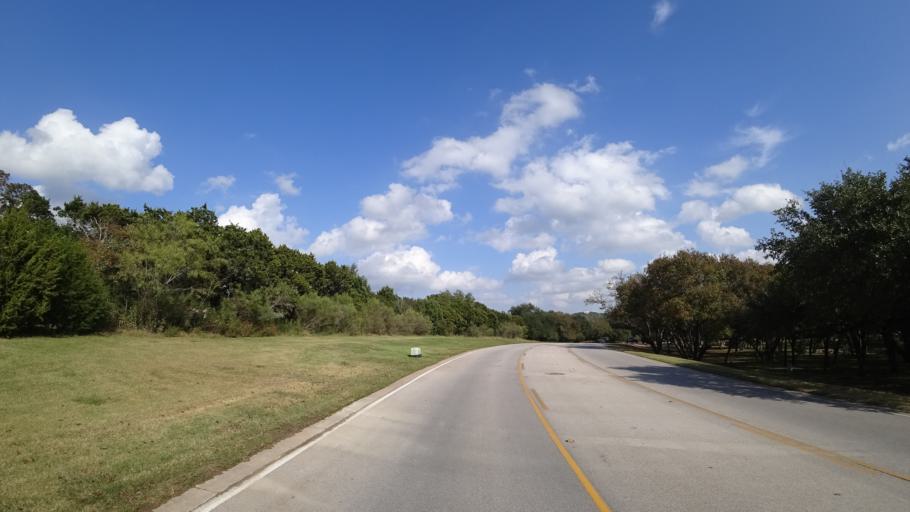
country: US
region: Texas
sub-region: Travis County
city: Lost Creek
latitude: 30.2975
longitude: -97.8565
